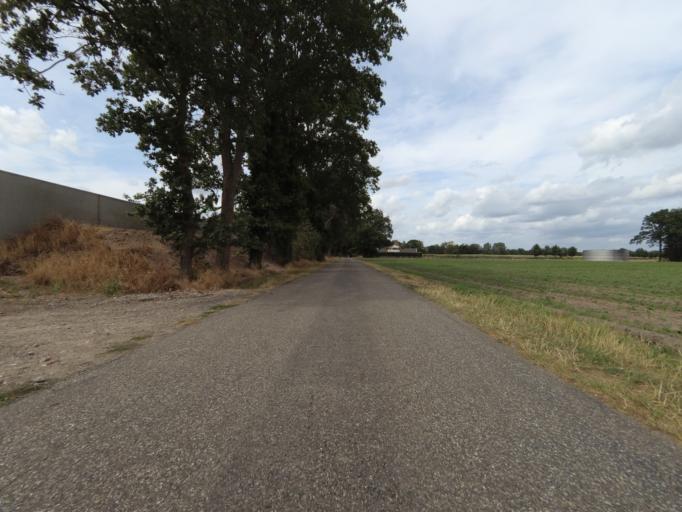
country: DE
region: North Rhine-Westphalia
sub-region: Regierungsbezirk Munster
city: Ahaus
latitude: 52.1231
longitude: 7.0092
